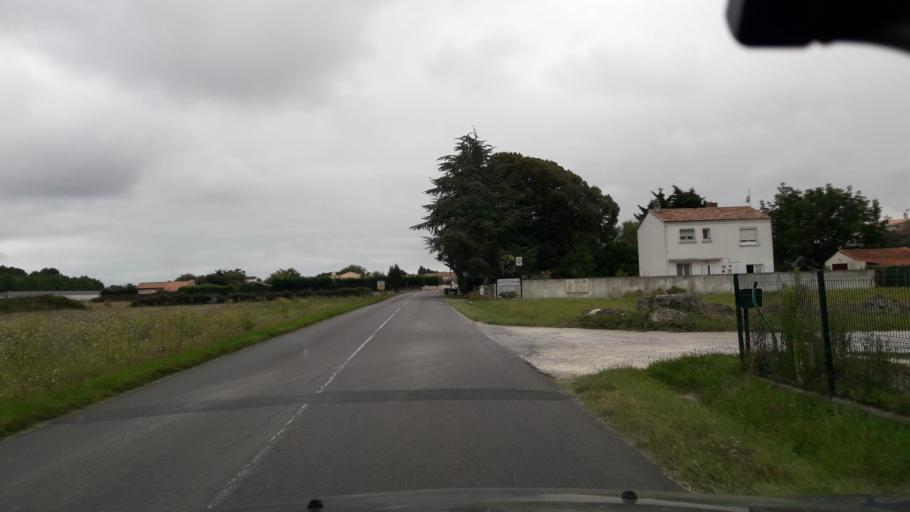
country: FR
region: Poitou-Charentes
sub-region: Departement de la Charente-Maritime
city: Les Mathes
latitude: 45.7263
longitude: -1.1407
